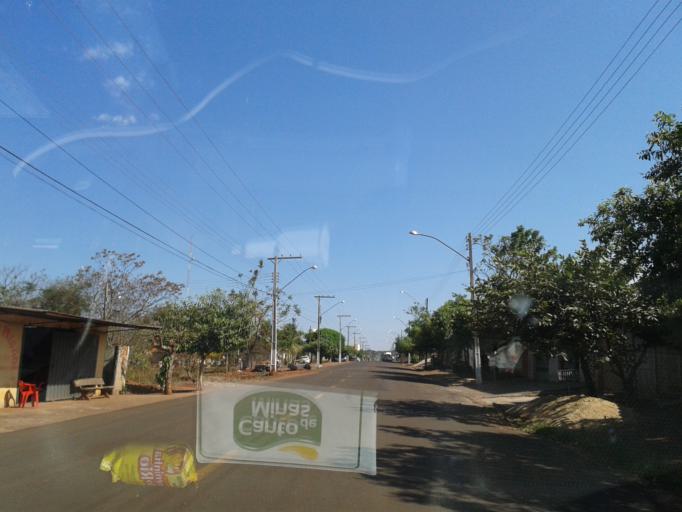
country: BR
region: Minas Gerais
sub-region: Santa Vitoria
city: Santa Vitoria
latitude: -19.0099
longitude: -50.5435
